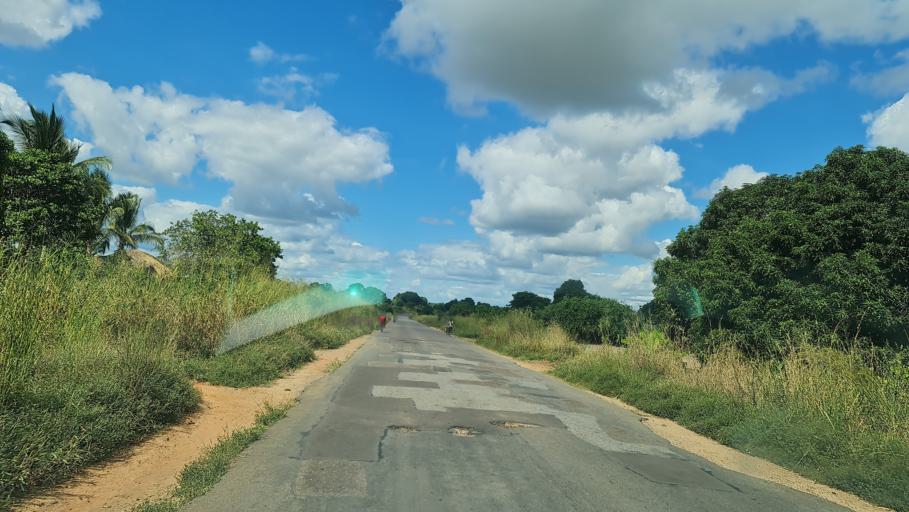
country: MZ
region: Zambezia
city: Quelimane
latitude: -17.5118
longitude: 36.2556
